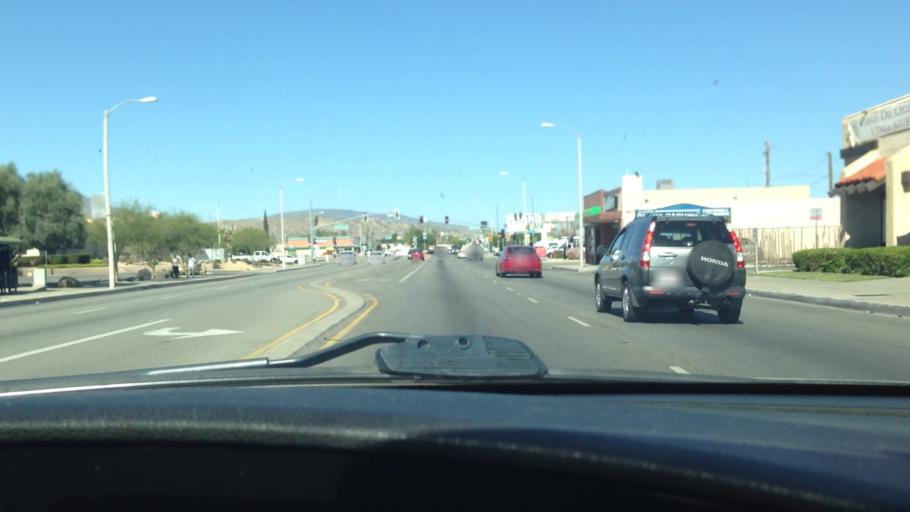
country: US
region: California
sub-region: Los Angeles County
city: Palmdale
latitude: 34.5794
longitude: -118.1165
